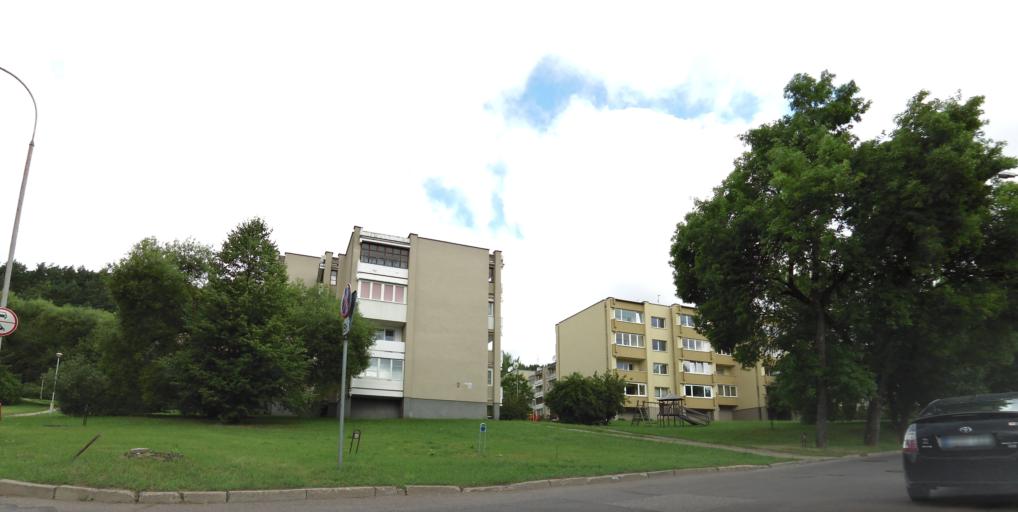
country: LT
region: Vilnius County
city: Seskine
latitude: 54.6946
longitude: 25.2384
